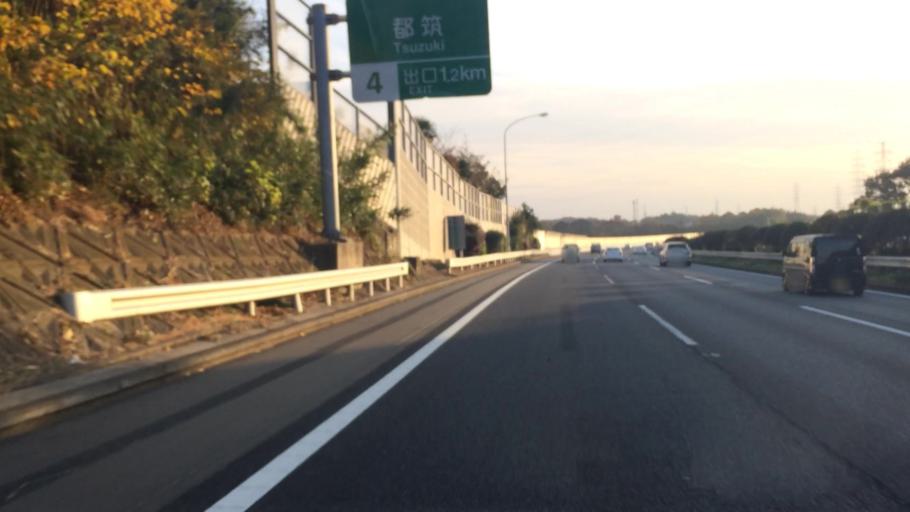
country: JP
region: Kanagawa
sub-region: Kawasaki-shi
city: Kawasaki
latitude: 35.5575
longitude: 139.6090
